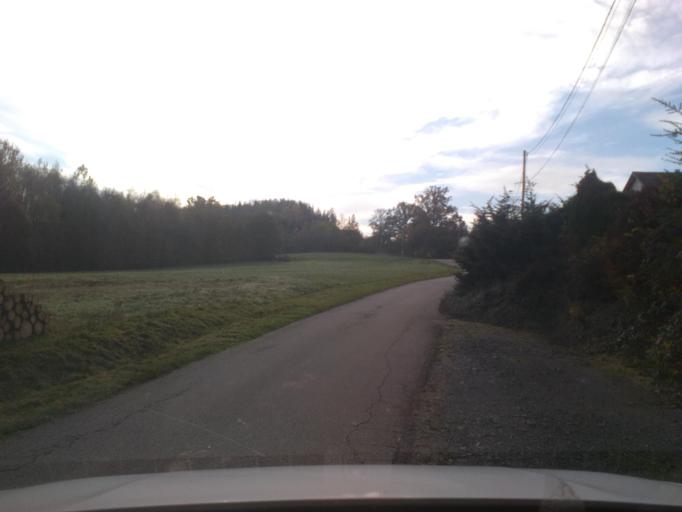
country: FR
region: Lorraine
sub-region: Departement des Vosges
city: Saint-Michel-sur-Meurthe
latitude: 48.3458
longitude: 6.8978
